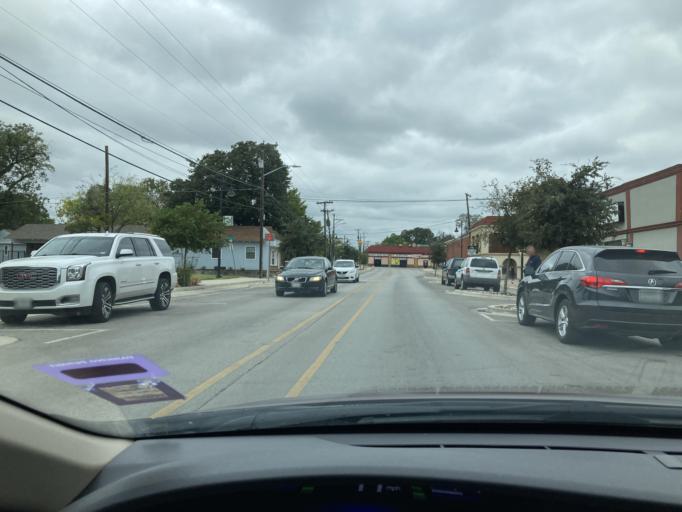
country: US
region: Texas
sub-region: Tarrant County
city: Haltom City
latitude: 32.7732
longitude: -97.3072
